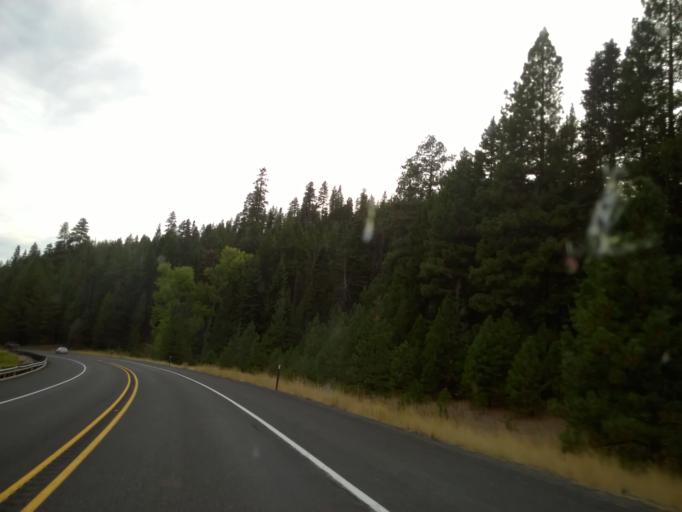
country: US
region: Washington
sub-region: Kittitas County
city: Cle Elum
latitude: 47.3184
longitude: -120.6924
